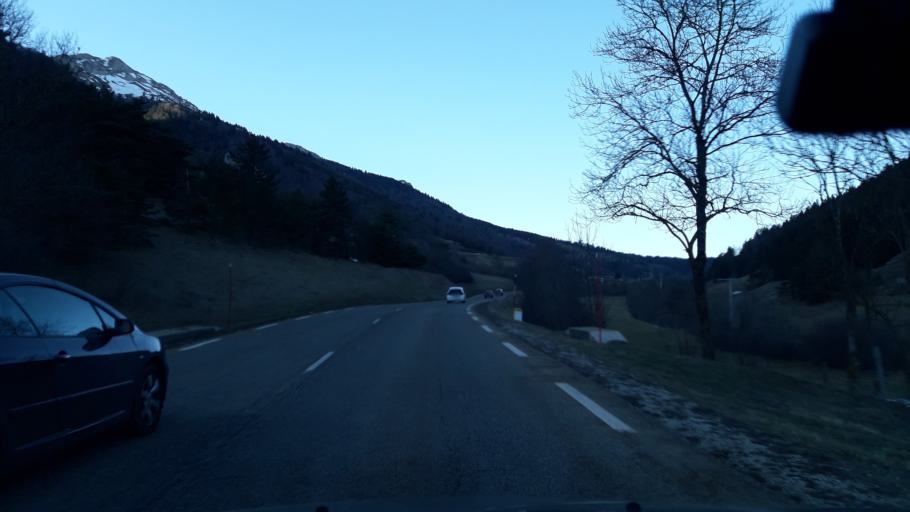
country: FR
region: Rhone-Alpes
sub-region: Departement de l'Isere
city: Mens
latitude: 44.7066
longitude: 5.6782
